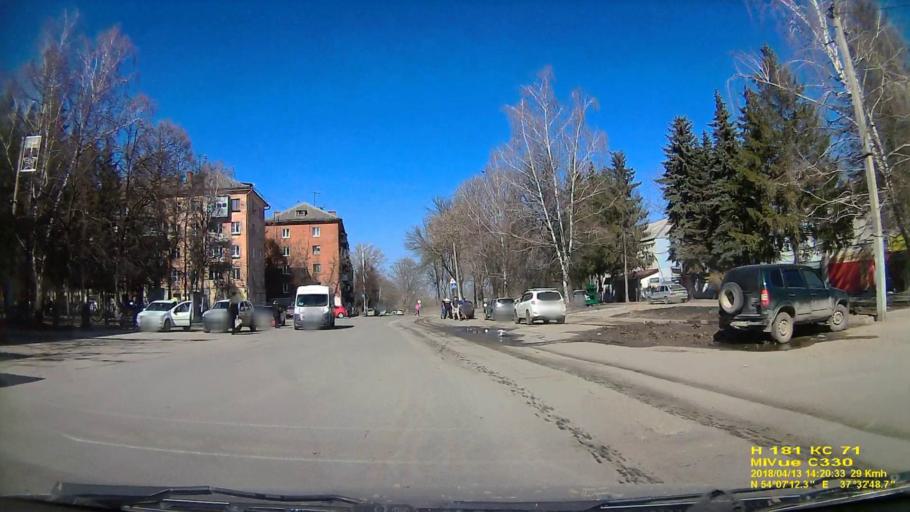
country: RU
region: Tula
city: Kosaya Gora
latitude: 54.1201
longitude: 37.5469
